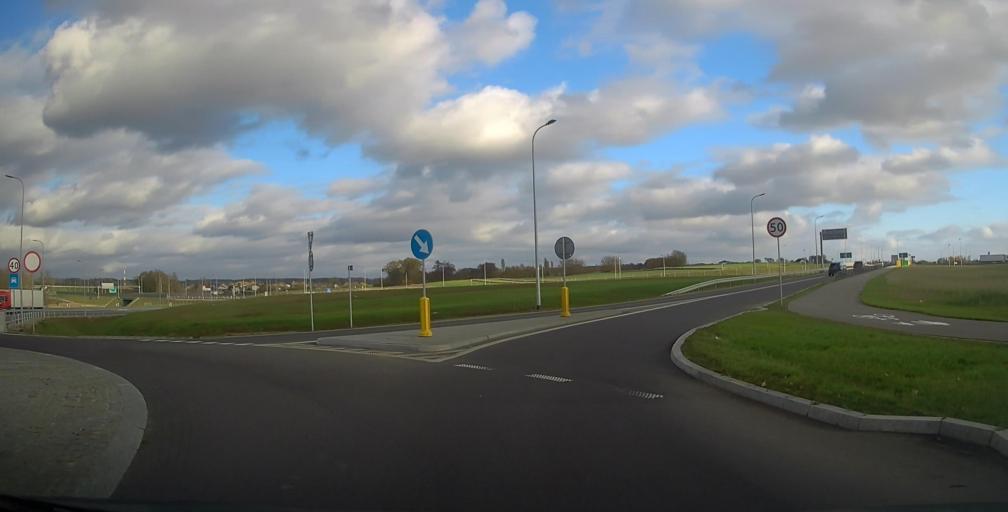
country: PL
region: Podlasie
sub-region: Powiat lomzynski
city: Piatnica
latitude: 53.2505
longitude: 22.1037
